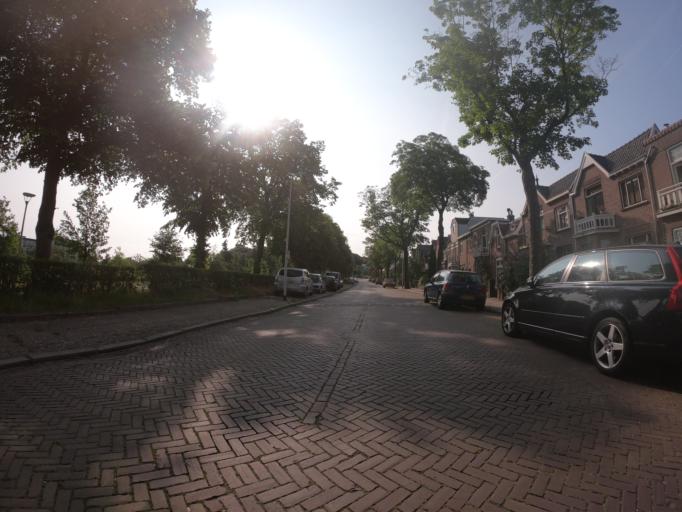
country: NL
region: Gelderland
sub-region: Gemeente Nijmegen
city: Nijmegen
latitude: 51.8320
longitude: 5.8746
